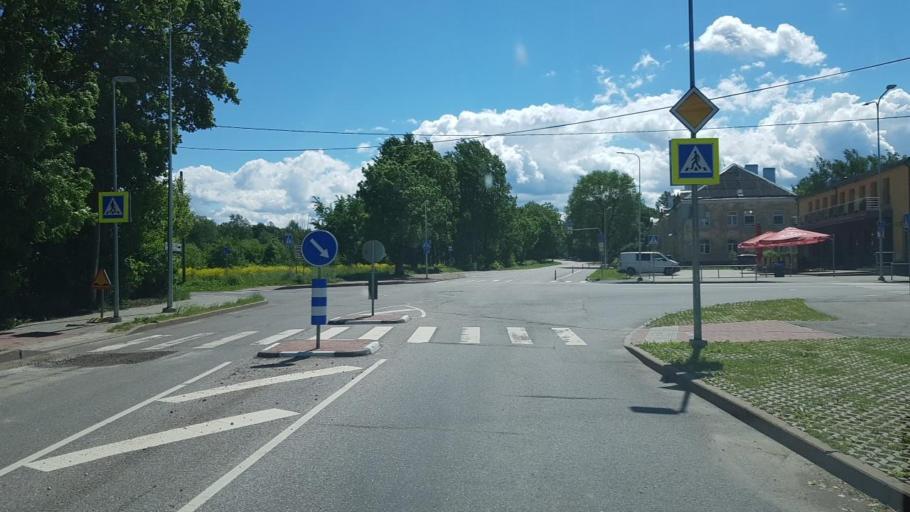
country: EE
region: Ida-Virumaa
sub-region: Narva linn
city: Narva
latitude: 59.3869
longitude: 28.1978
